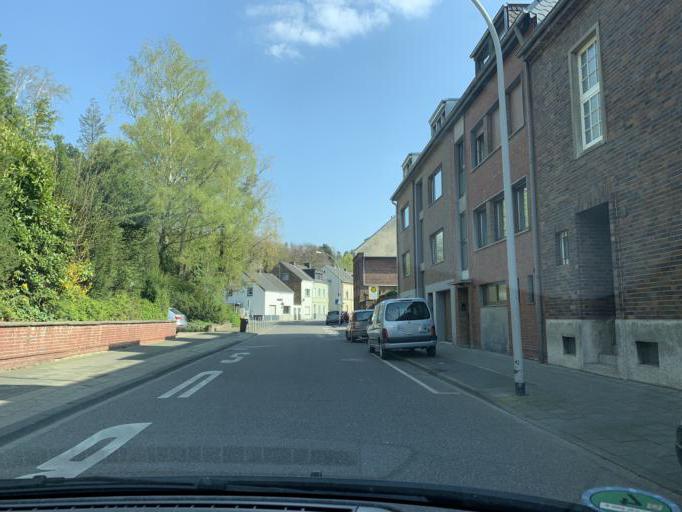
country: DE
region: North Rhine-Westphalia
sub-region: Regierungsbezirk Dusseldorf
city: Juchen
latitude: 51.1311
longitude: 6.4586
